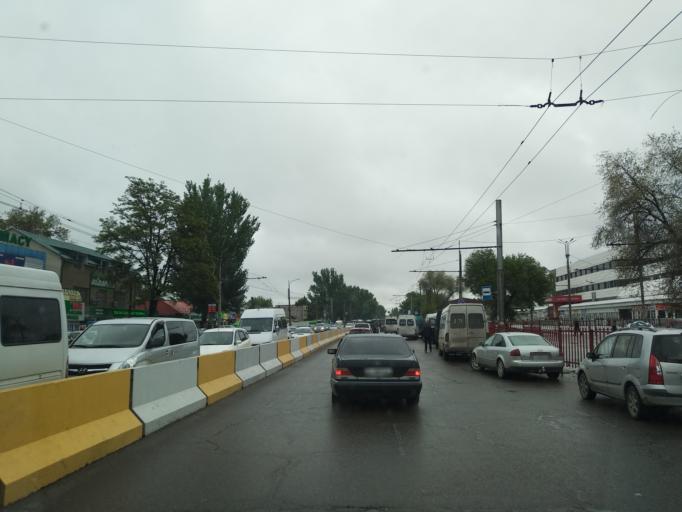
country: KG
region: Chuy
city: Lebedinovka
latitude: 42.8882
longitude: 74.6369
